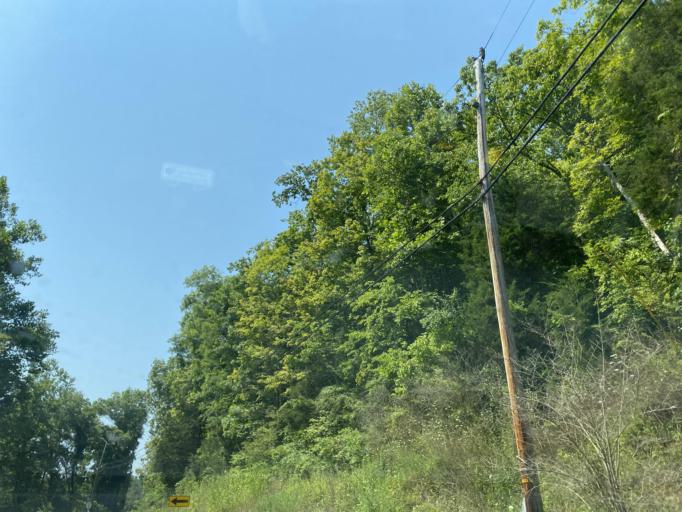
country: US
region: Kentucky
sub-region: Campbell County
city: Claryville
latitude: 38.8479
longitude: -84.4683
